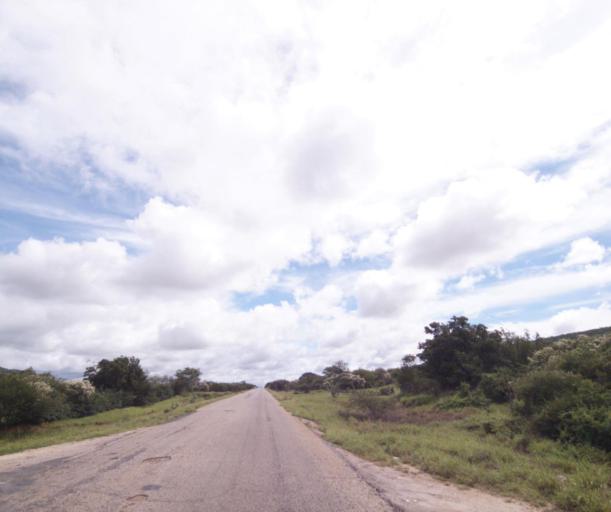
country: BR
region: Bahia
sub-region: Brumado
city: Brumado
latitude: -14.1906
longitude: -41.5776
